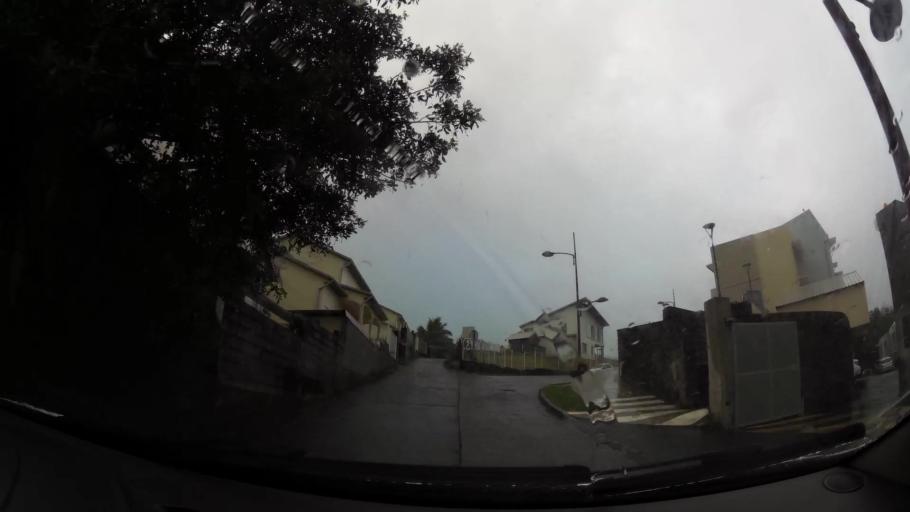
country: RE
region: Reunion
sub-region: Reunion
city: Saint-Benoit
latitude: -21.0309
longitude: 55.6910
